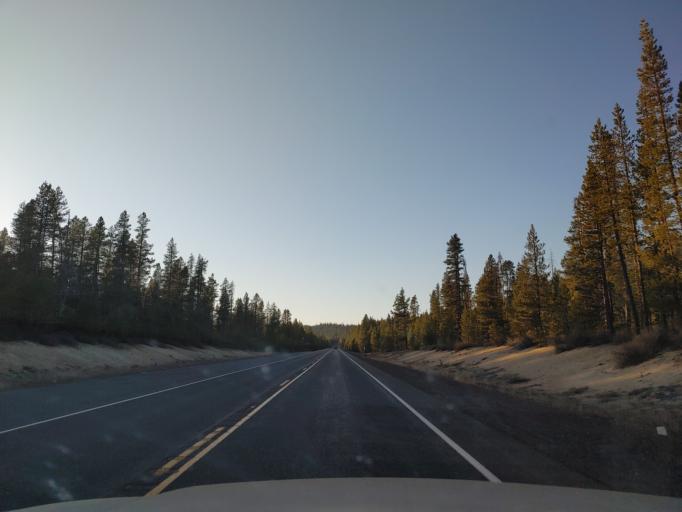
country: US
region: Oregon
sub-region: Deschutes County
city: La Pine
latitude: 43.4347
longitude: -121.8582
